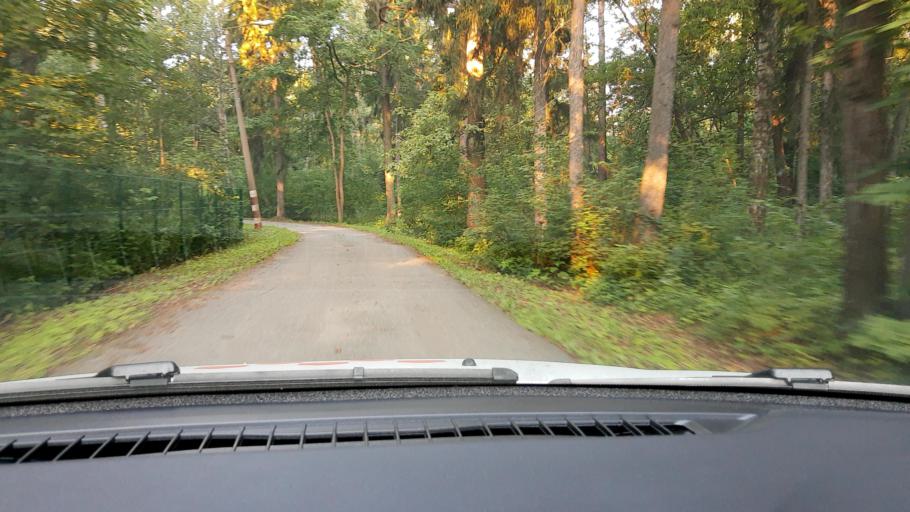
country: RU
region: Nizjnij Novgorod
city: Afonino
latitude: 56.1797
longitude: 44.0746
